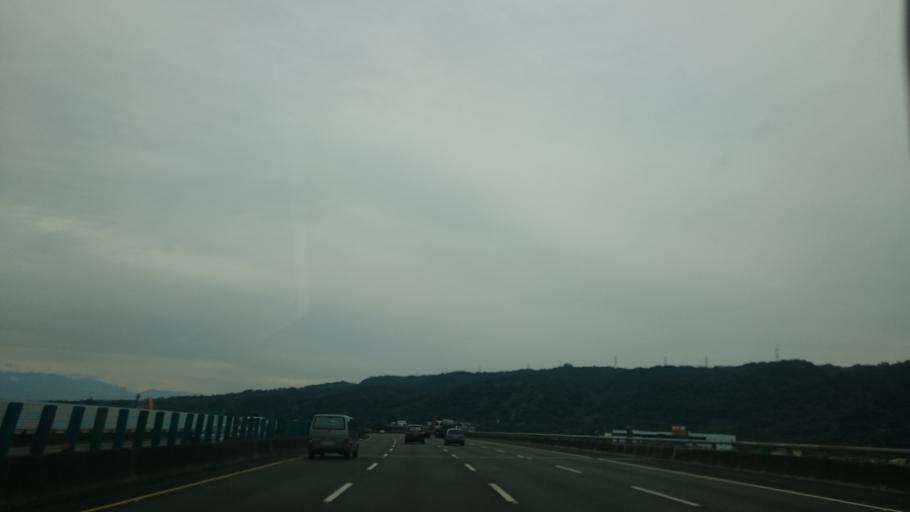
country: TW
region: Taiwan
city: Zhongxing New Village
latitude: 23.9721
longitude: 120.6488
